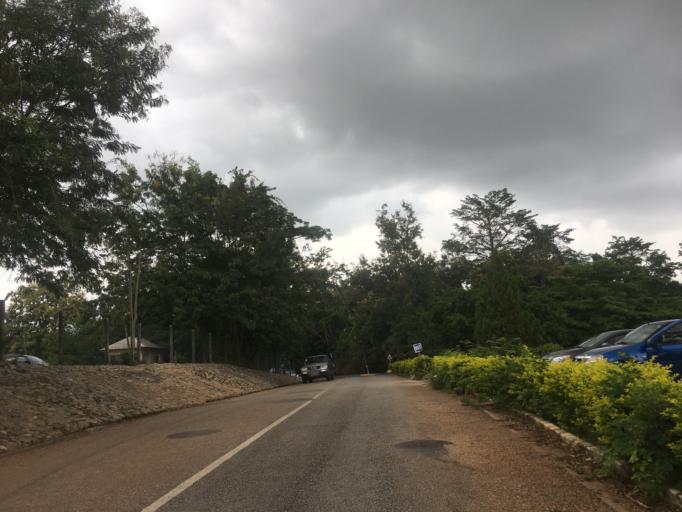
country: GH
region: Ashanti
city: Mamponteng
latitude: 6.6850
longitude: -1.5688
